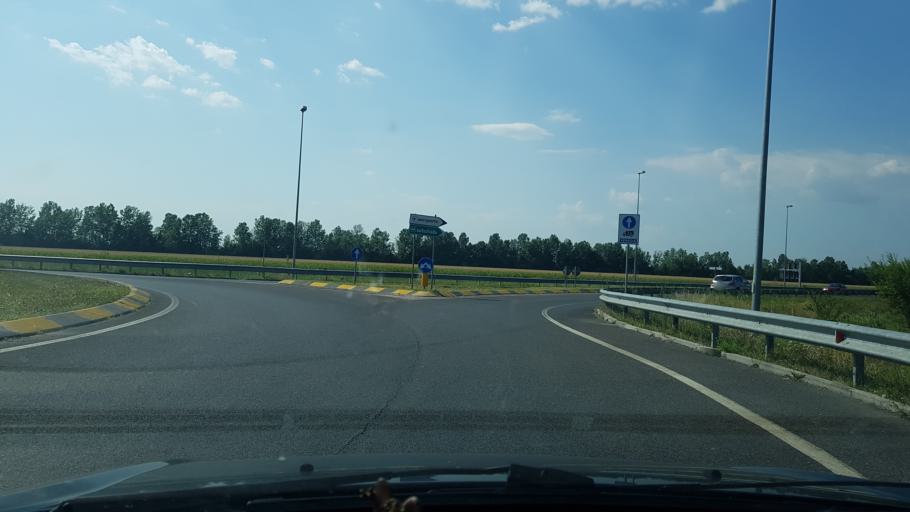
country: IT
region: Friuli Venezia Giulia
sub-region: Provincia di Gorizia
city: Staranzano
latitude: 45.7938
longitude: 13.4894
